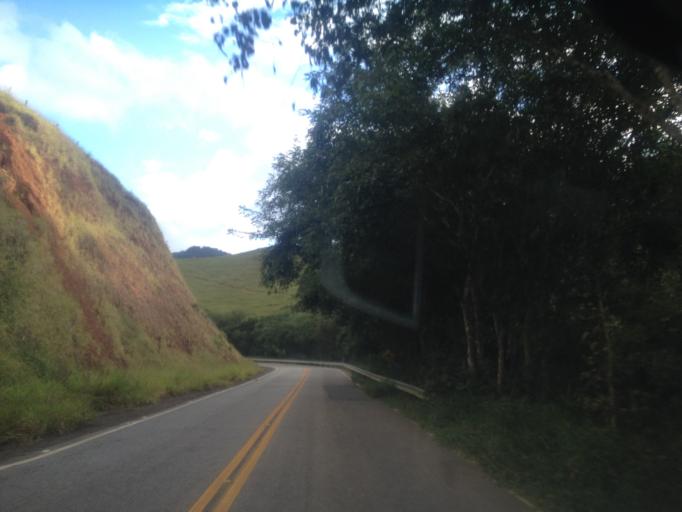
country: BR
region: Rio de Janeiro
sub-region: Quatis
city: Quatis
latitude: -22.2999
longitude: -44.2586
